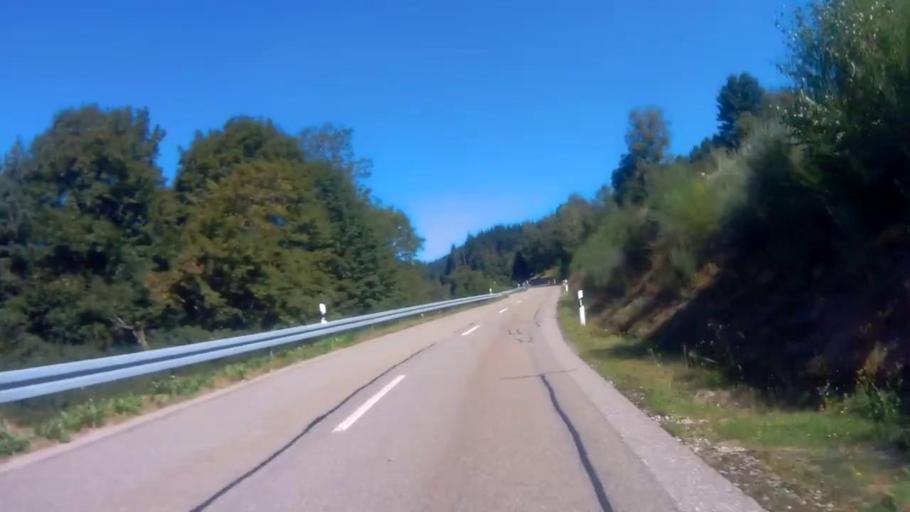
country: DE
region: Baden-Wuerttemberg
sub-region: Freiburg Region
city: Bollen
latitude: 47.7576
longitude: 7.7574
